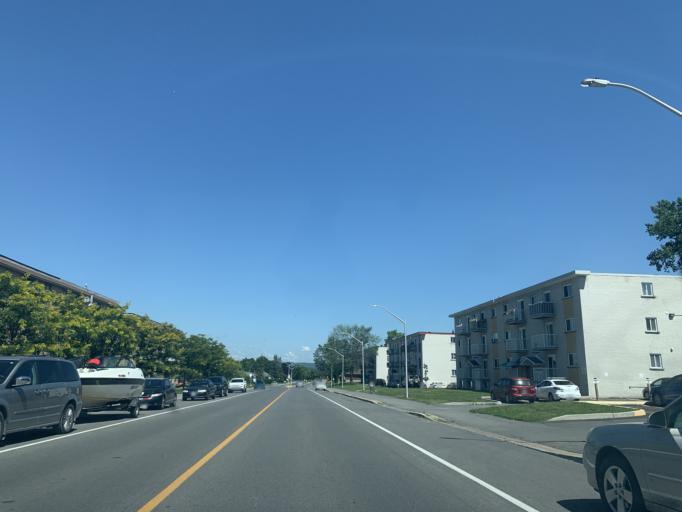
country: CA
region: Ontario
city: Hawkesbury
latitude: 45.6007
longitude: -74.6121
